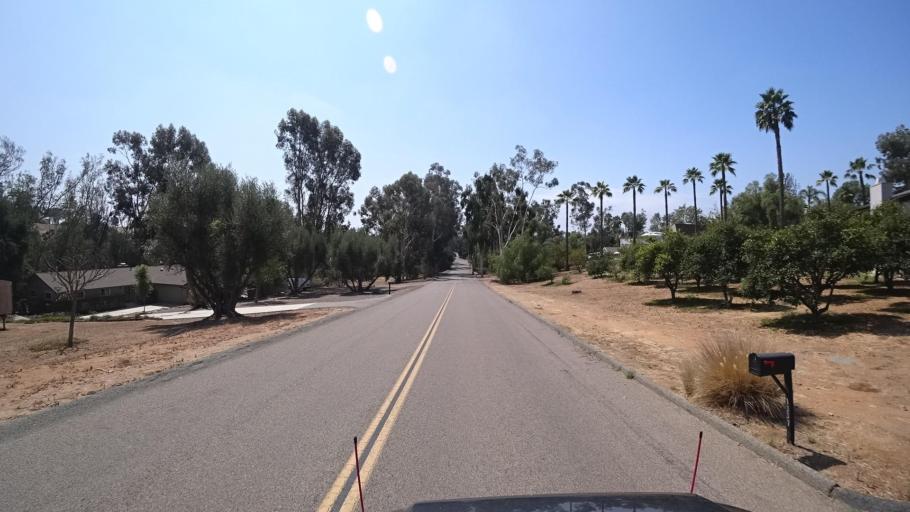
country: US
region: California
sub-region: San Diego County
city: Fallbrook
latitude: 33.3644
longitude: -117.2363
